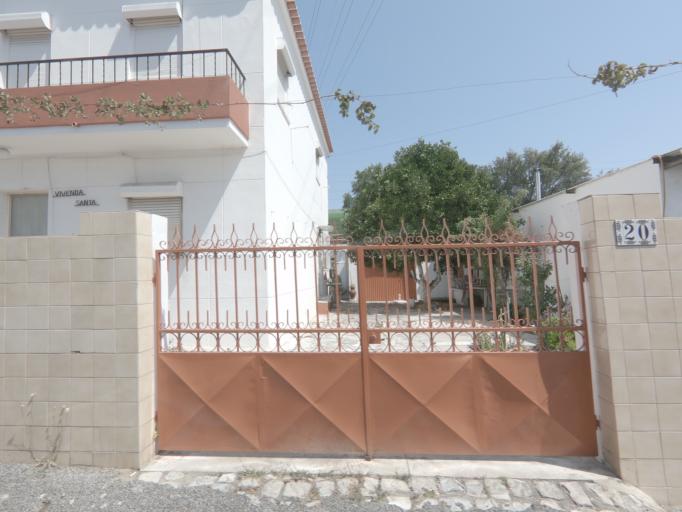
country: PT
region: Setubal
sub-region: Setubal
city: Setubal
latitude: 38.5443
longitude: -8.8826
